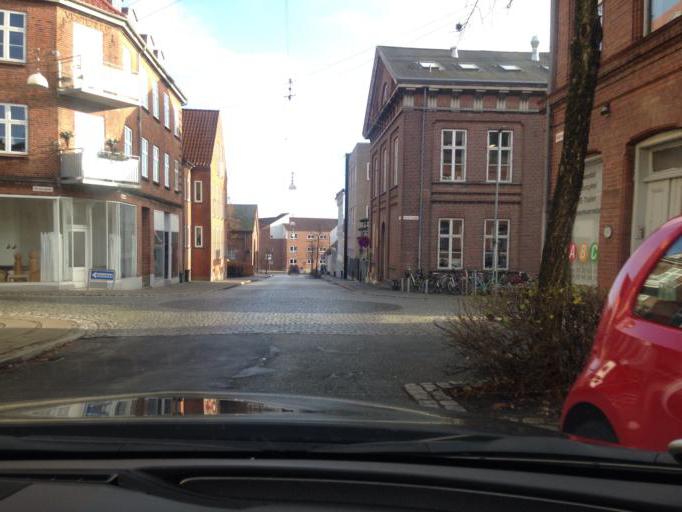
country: DK
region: South Denmark
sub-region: Kolding Kommune
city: Kolding
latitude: 55.4909
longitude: 9.4684
